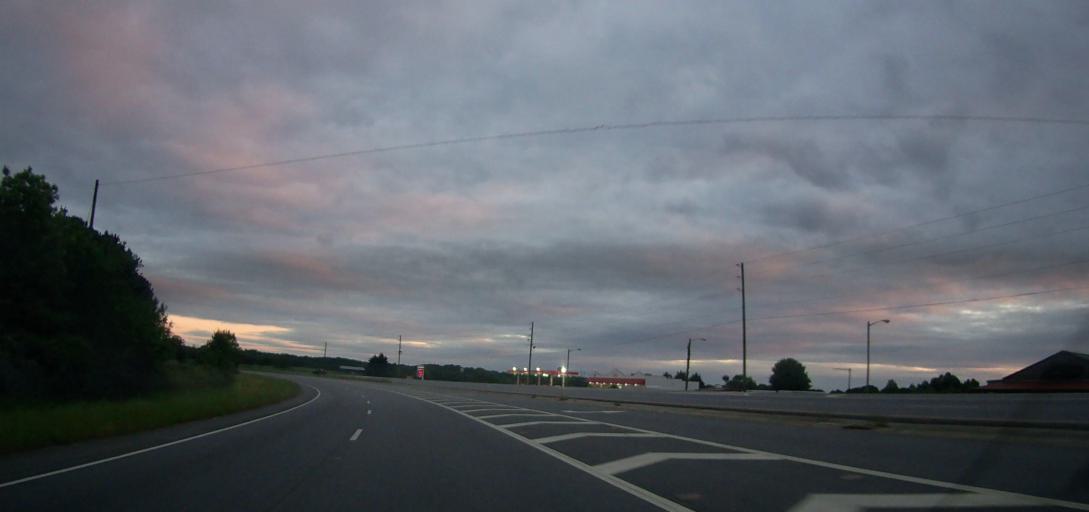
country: US
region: Georgia
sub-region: Jackson County
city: Arcade
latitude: 34.0370
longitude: -83.5002
